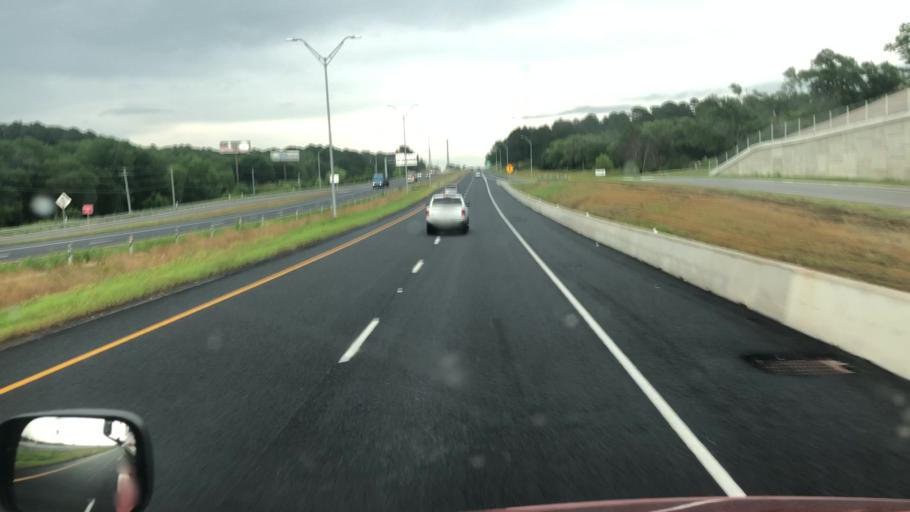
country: US
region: Texas
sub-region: Bastrop County
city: Bastrop
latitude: 30.1049
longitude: -97.3055
